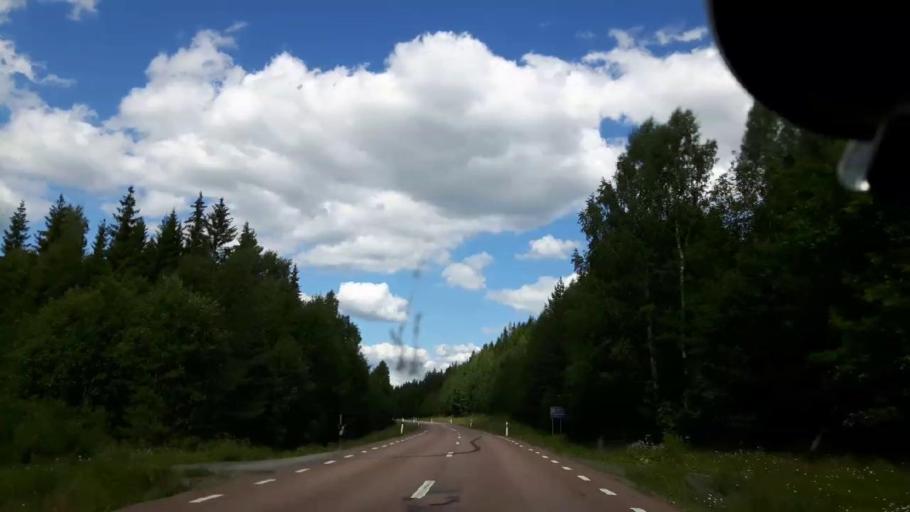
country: SE
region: Jaemtland
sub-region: Ragunda Kommun
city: Hammarstrand
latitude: 62.9204
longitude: 16.7039
